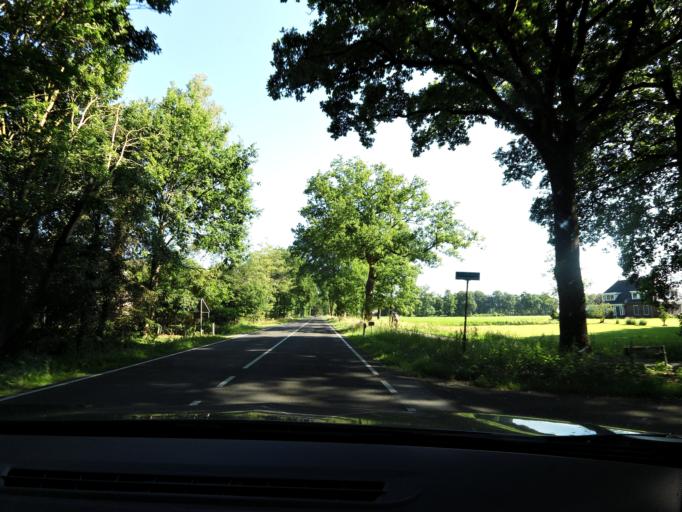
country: NL
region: Overijssel
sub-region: Gemeente Twenterand
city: Den Ham
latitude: 52.4181
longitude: 6.4421
